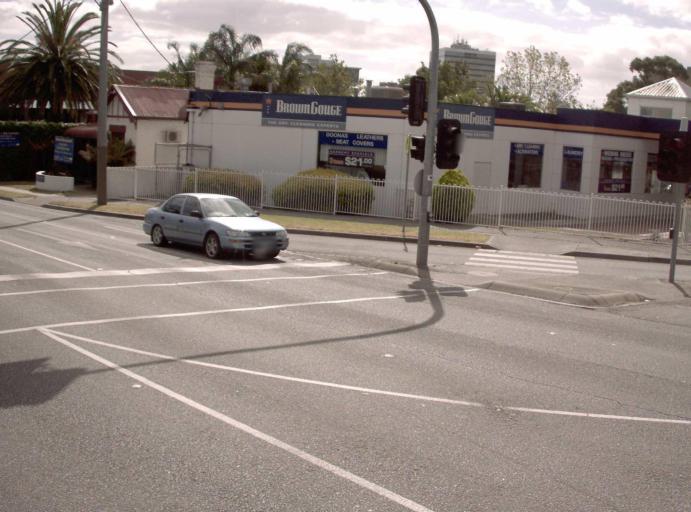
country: AU
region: Victoria
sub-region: Greater Dandenong
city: Dandenong
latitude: -37.9887
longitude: 145.2181
